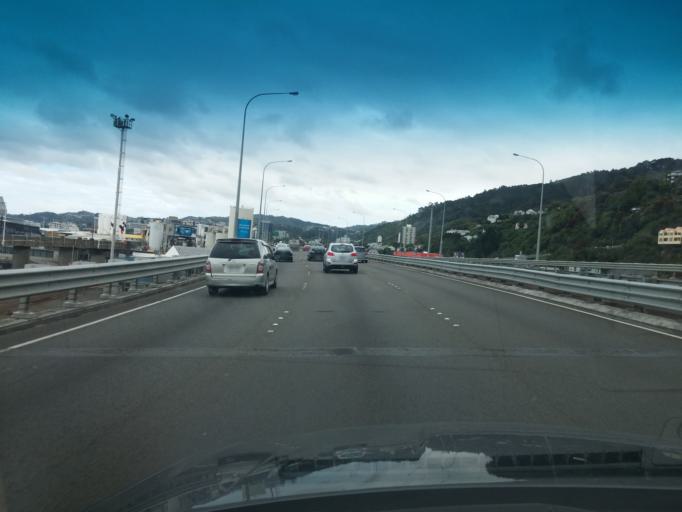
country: NZ
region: Wellington
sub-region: Wellington City
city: Wellington
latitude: -41.2628
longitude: 174.7880
